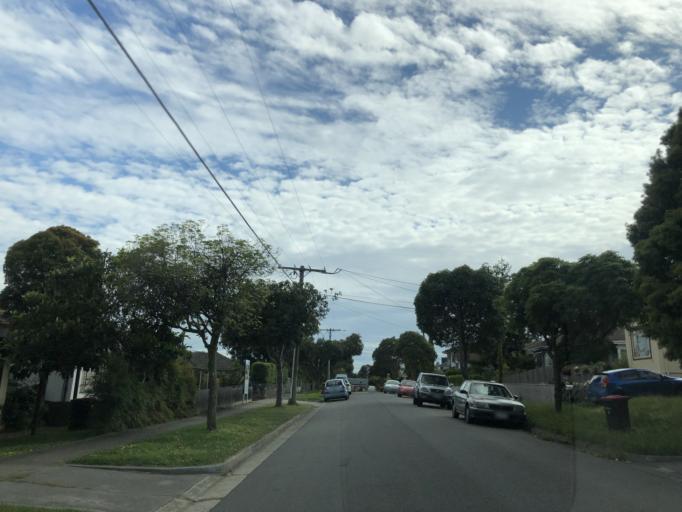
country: AU
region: Victoria
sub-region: Greater Dandenong
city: Dandenong
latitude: -37.9779
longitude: 145.2006
